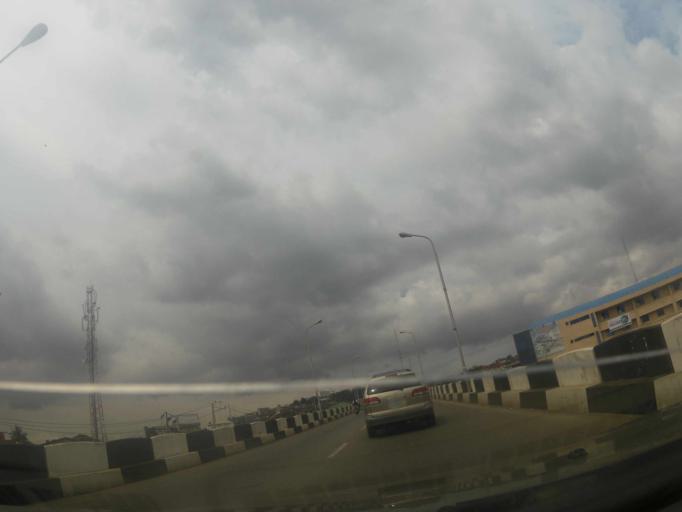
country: NG
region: Oyo
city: Ibadan
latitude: 7.3998
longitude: 3.8895
